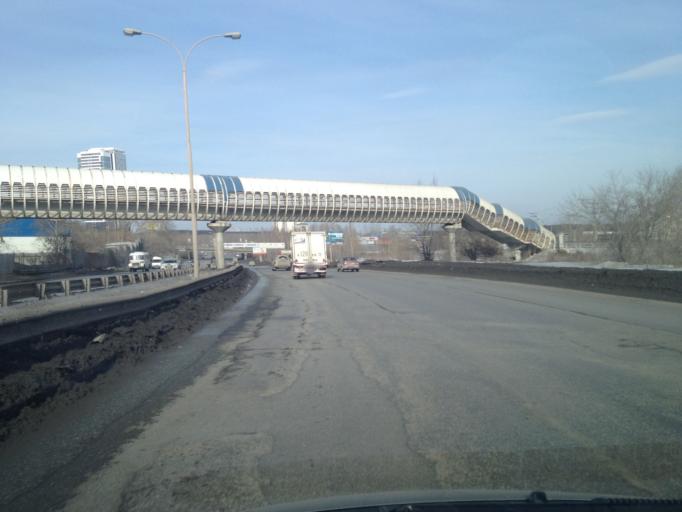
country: RU
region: Sverdlovsk
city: Yekaterinburg
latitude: 56.7917
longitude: 60.6388
